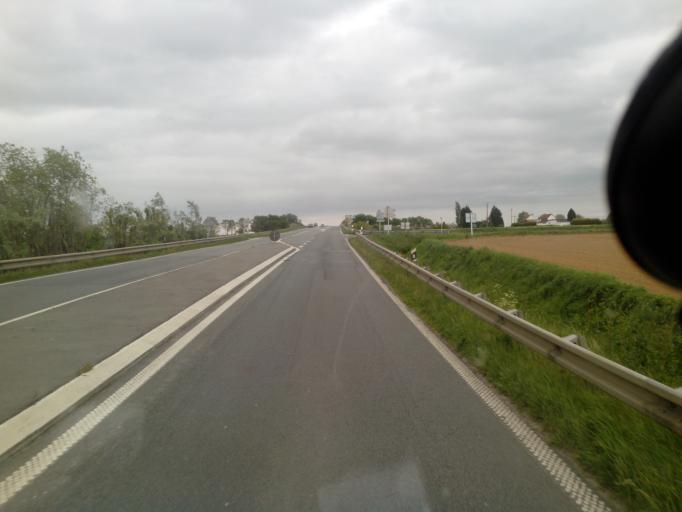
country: FR
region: Nord-Pas-de-Calais
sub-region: Departement du Nord
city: Meteren
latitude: 50.7329
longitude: 2.6892
